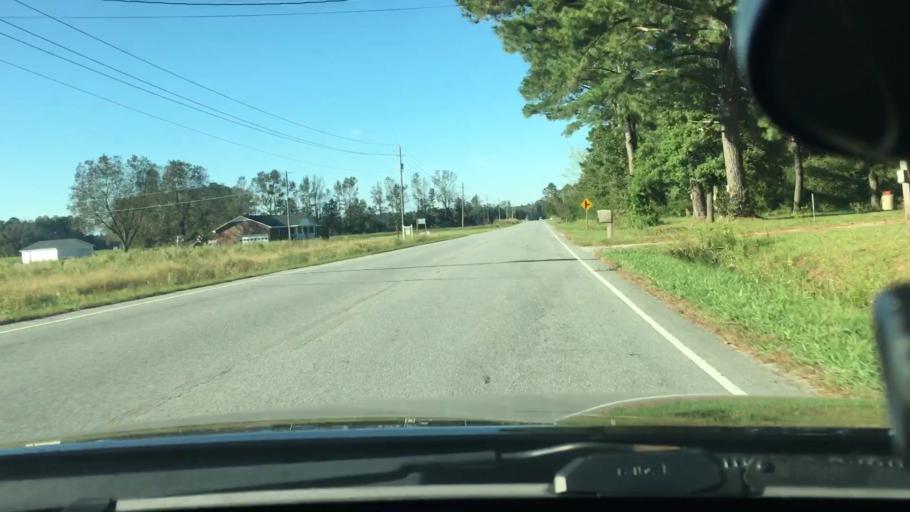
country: US
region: North Carolina
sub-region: Craven County
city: Vanceboro
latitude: 35.4243
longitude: -77.2606
